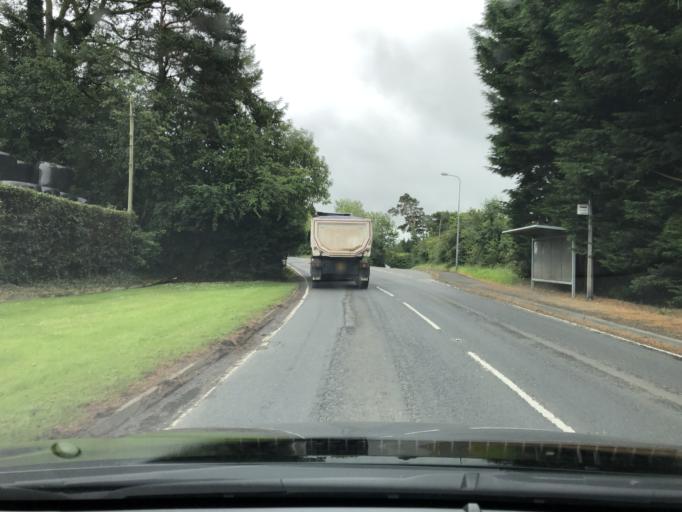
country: GB
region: Northern Ireland
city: Ballynahinch
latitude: 54.3644
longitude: -5.8607
